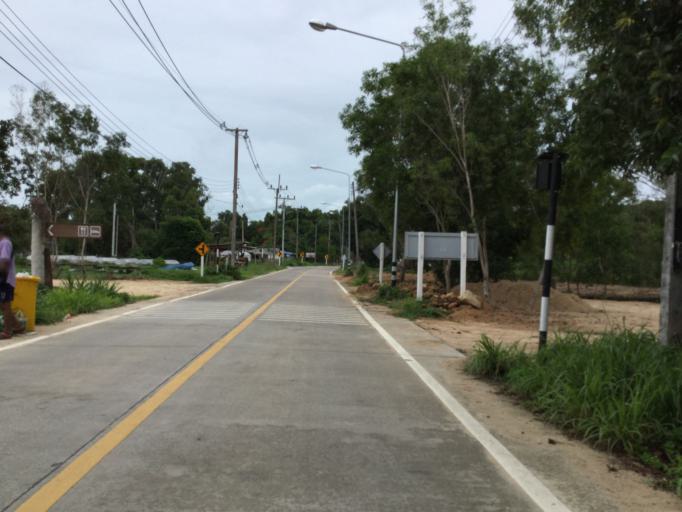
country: TH
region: Surat Thani
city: Ko Pha-Ngan
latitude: 9.7183
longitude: 100.0005
